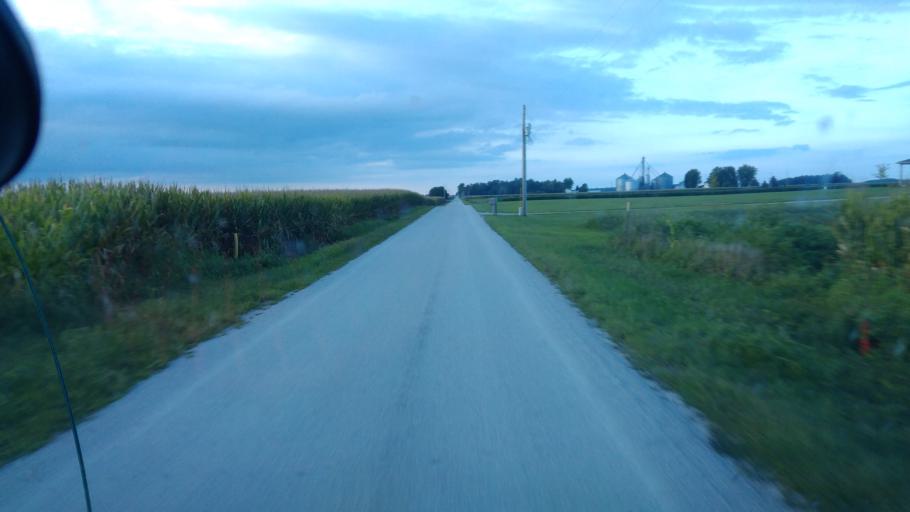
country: US
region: Ohio
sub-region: Hardin County
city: Kenton
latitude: 40.6539
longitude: -83.5149
